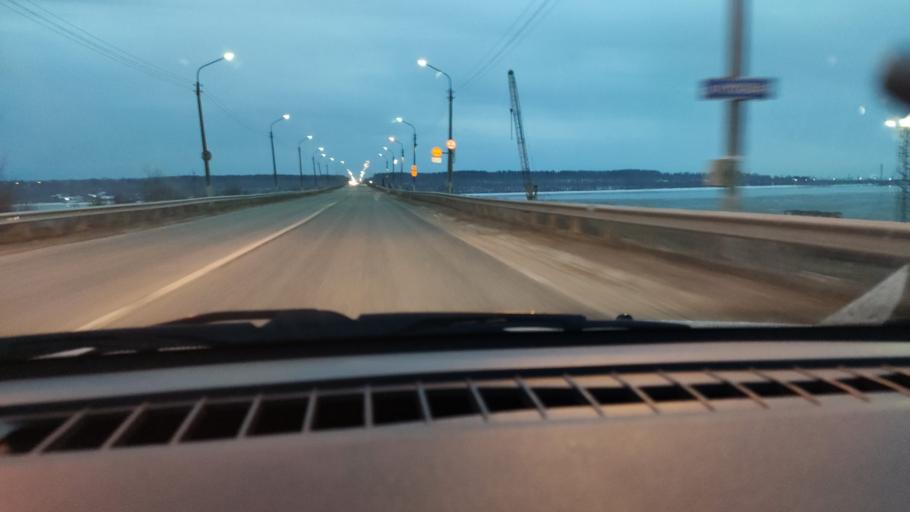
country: RU
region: Perm
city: Polazna
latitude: 58.1734
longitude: 56.4148
